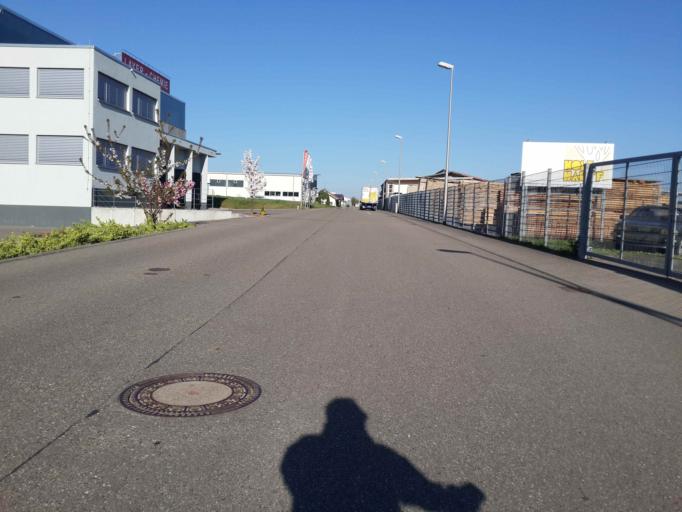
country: DE
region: Baden-Wuerttemberg
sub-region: Regierungsbezirk Stuttgart
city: Leingarten
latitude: 49.1512
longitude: 9.1273
